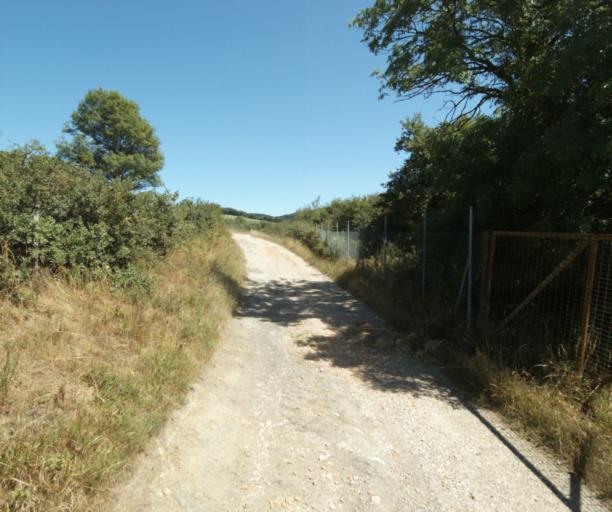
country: FR
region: Midi-Pyrenees
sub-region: Departement du Tarn
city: Soreze
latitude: 43.4436
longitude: 2.0894
